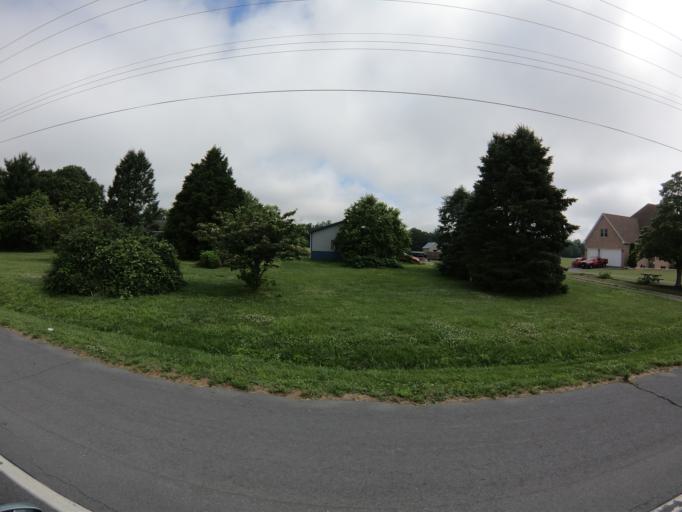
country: US
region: Delaware
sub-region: Kent County
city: Felton
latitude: 39.0057
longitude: -75.5430
